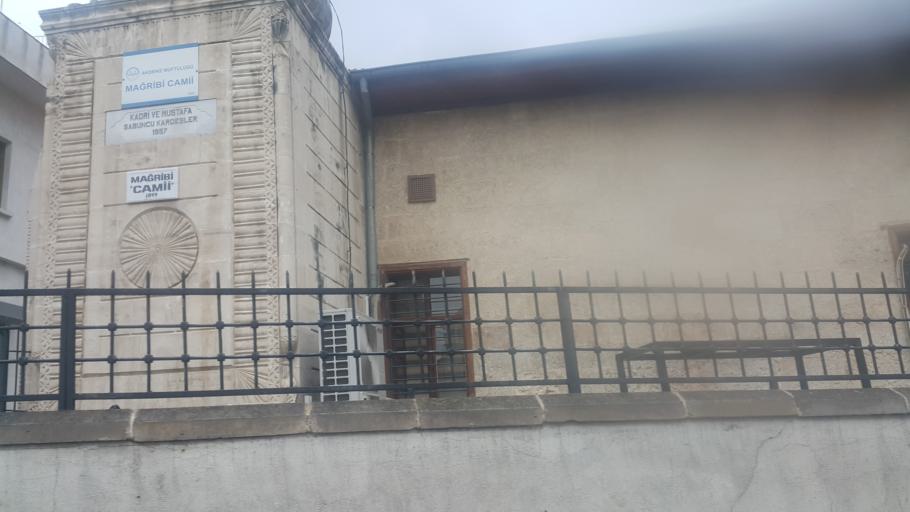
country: TR
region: Mersin
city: Mercin
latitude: 36.8023
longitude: 34.6282
